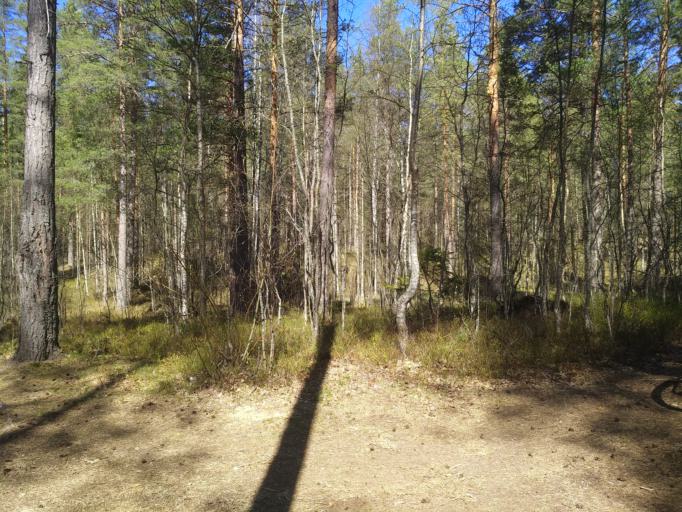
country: RU
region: Leningrad
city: Sapernoye
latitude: 60.6268
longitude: 30.0348
